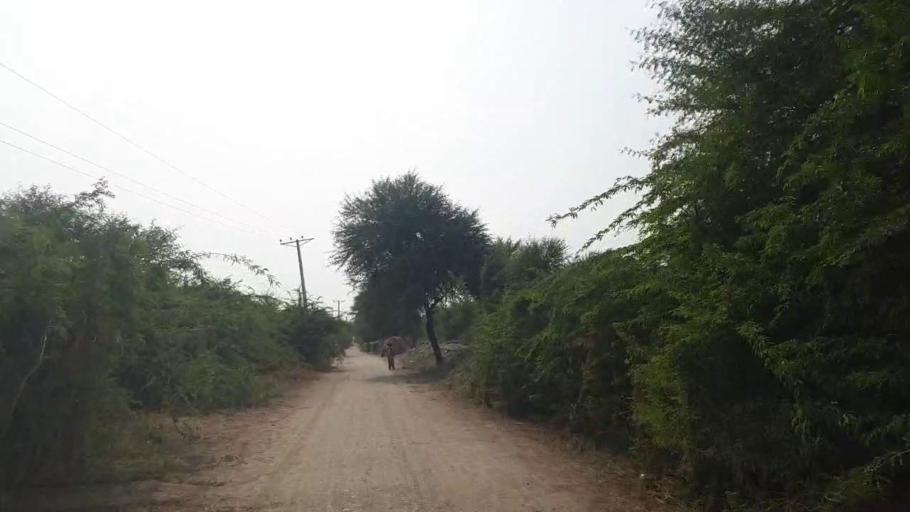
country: PK
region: Sindh
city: Badin
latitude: 24.6197
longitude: 68.7237
